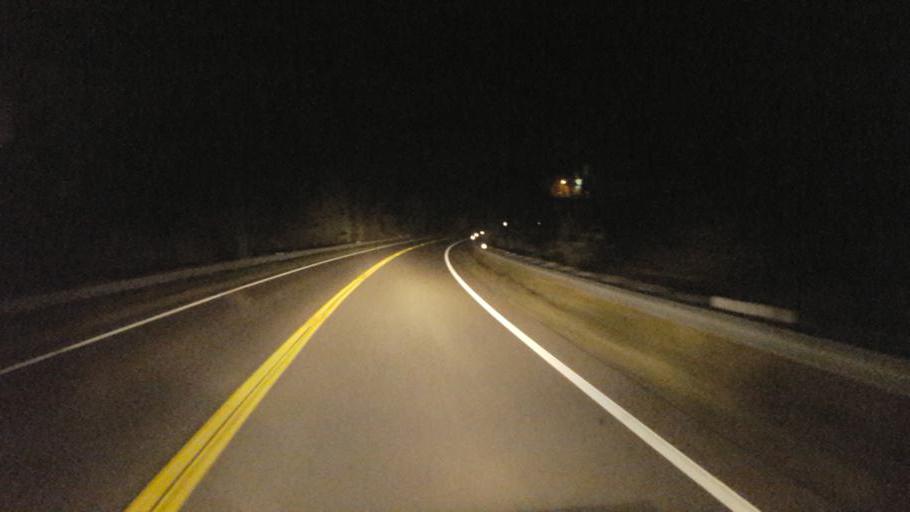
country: US
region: Ohio
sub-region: Harrison County
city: Cadiz
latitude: 40.3335
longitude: -81.1539
